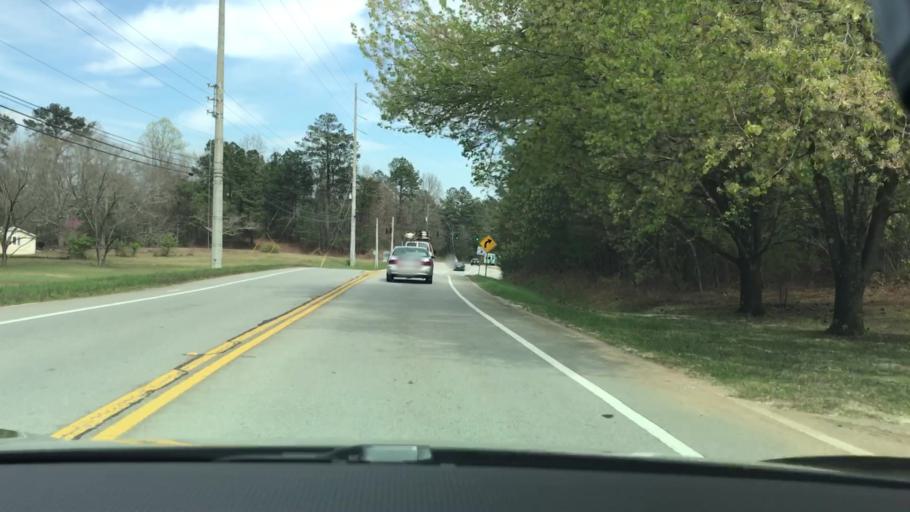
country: US
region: Georgia
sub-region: Gwinnett County
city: Sugar Hill
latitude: 34.1501
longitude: -84.0438
